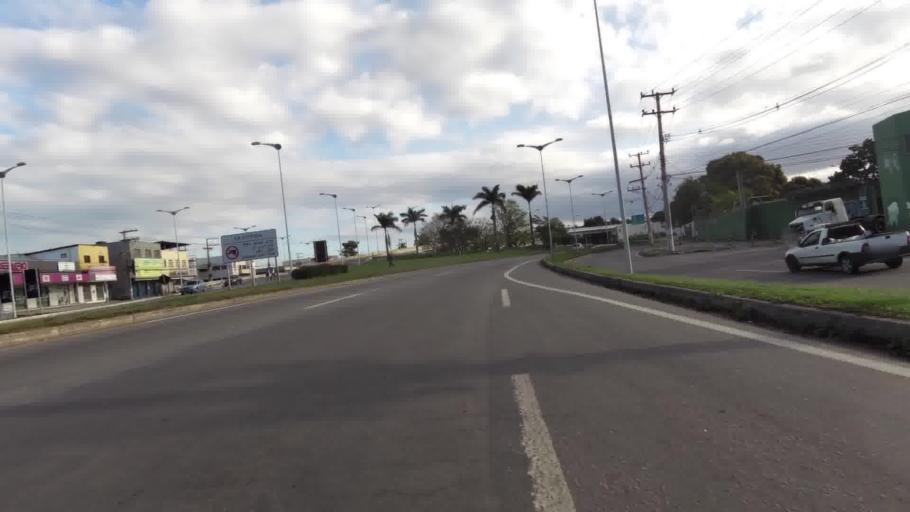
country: BR
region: Espirito Santo
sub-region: Vila Velha
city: Vila Velha
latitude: -20.2316
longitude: -40.2740
